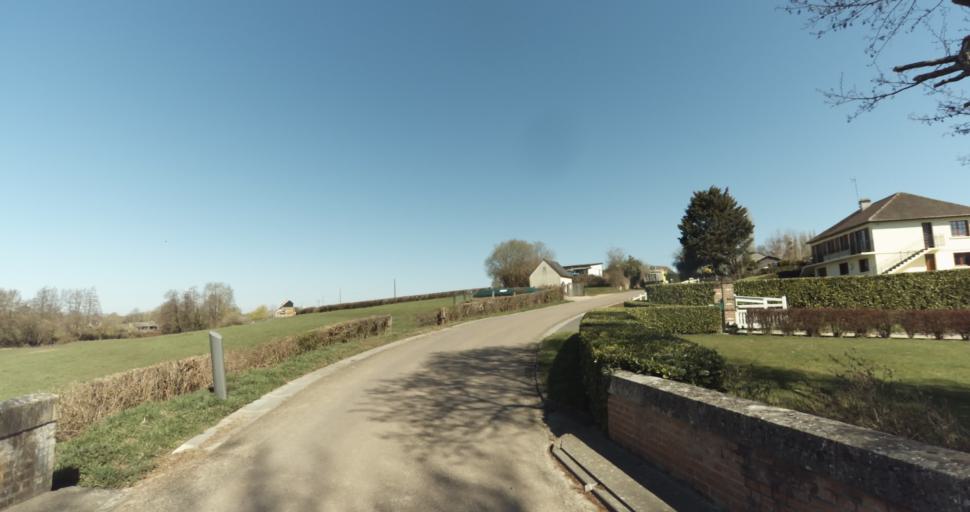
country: FR
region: Lower Normandy
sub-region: Departement du Calvados
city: Livarot
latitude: 49.0130
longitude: 0.0745
